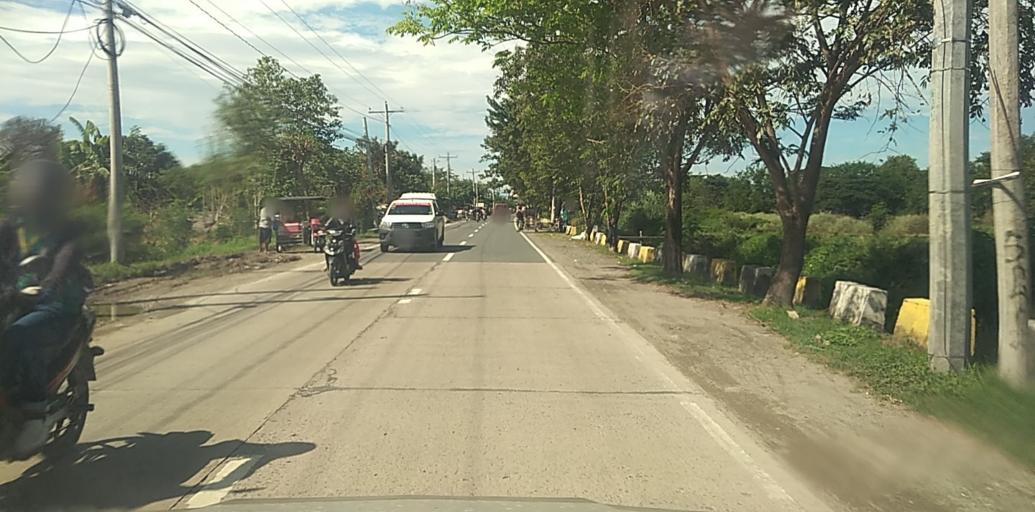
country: PH
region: Central Luzon
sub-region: Province of Pampanga
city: Arayat
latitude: 15.1500
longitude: 120.7505
